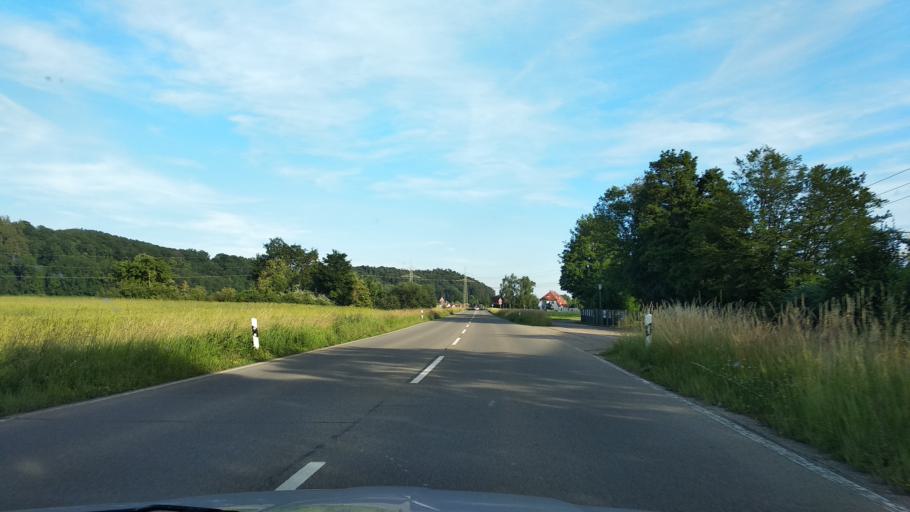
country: DE
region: Bavaria
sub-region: Swabia
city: Vohringen
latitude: 48.2694
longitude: 10.0846
